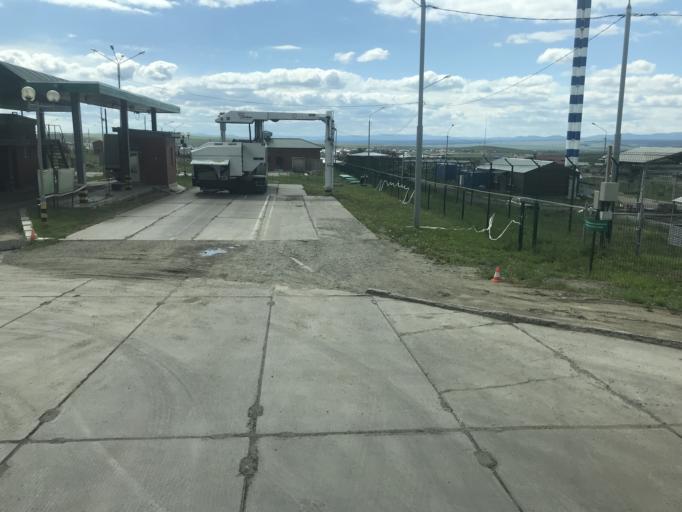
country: MN
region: Selenge
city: Altanbulag
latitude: 50.3253
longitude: 106.4869
